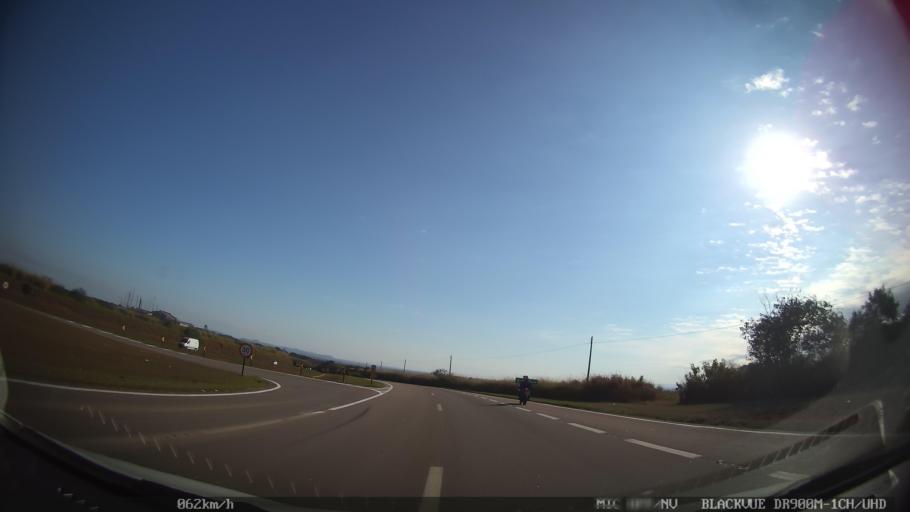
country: BR
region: Sao Paulo
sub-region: Piracicaba
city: Piracicaba
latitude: -22.6620
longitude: -47.6116
